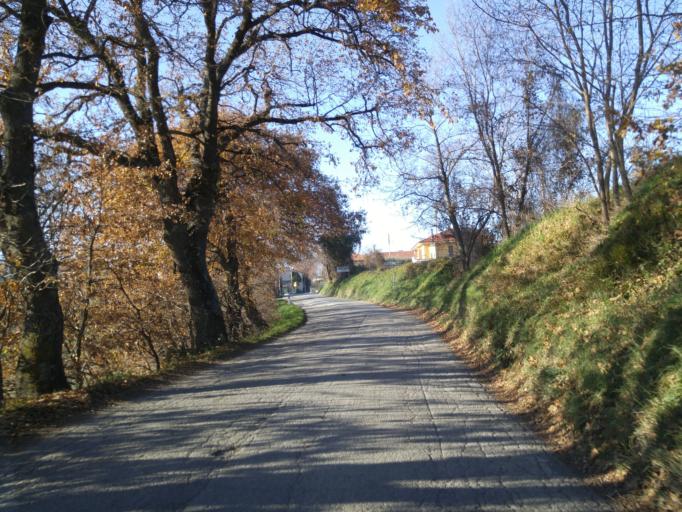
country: IT
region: The Marches
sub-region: Provincia di Pesaro e Urbino
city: Montefelcino
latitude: 43.7438
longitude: 12.8307
